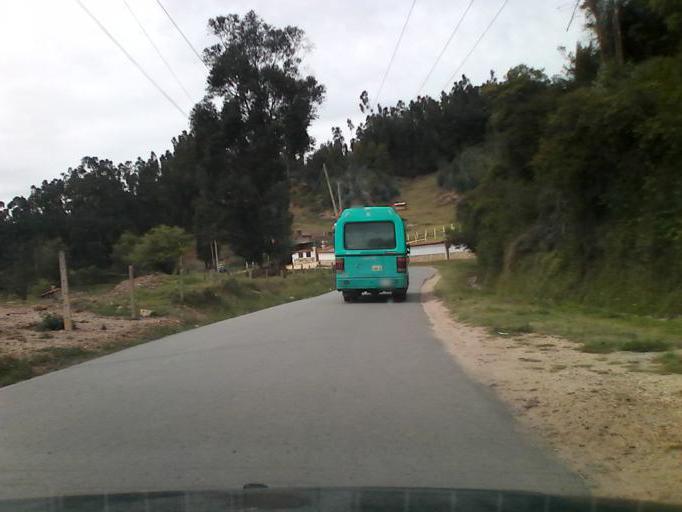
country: CO
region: Boyaca
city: Duitama
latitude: 5.7907
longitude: -73.0599
